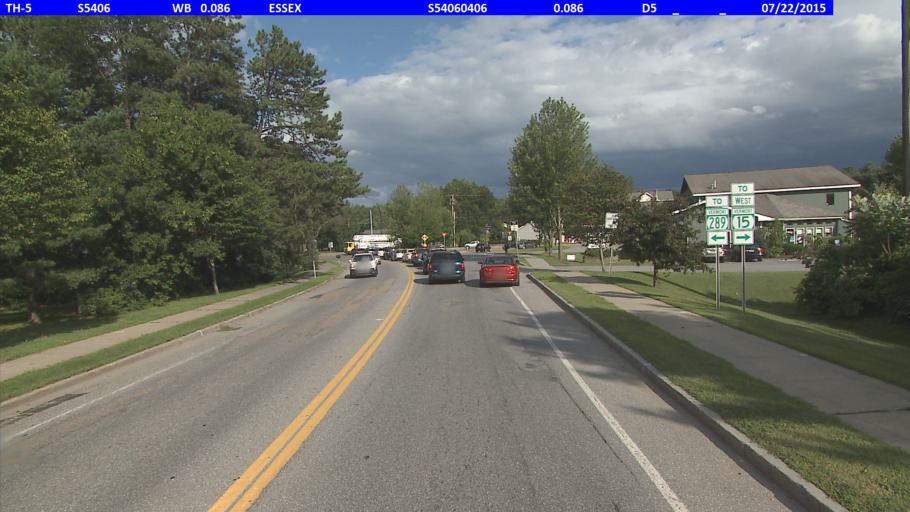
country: US
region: Vermont
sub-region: Chittenden County
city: Essex Junction
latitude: 44.5098
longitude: -73.1333
